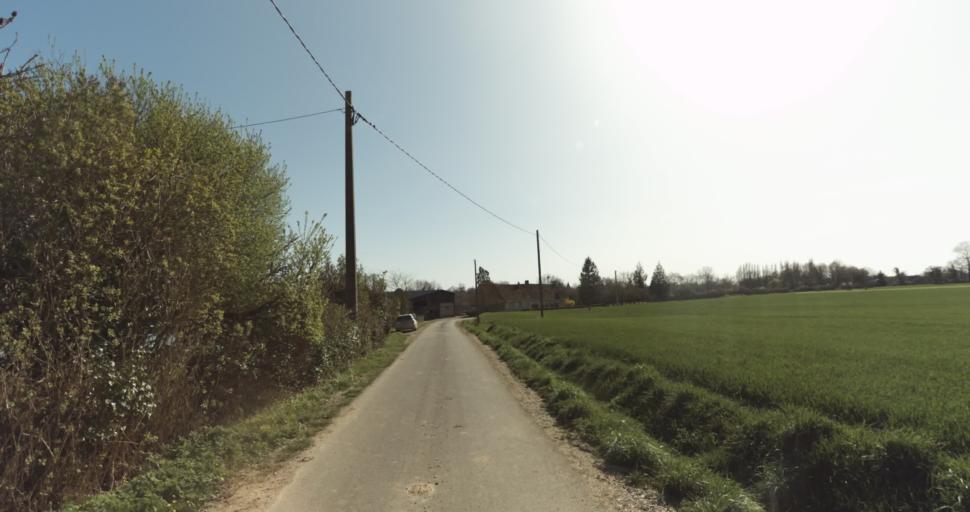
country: FR
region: Lower Normandy
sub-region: Departement du Calvados
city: Saint-Pierre-sur-Dives
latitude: 48.9382
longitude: 0.0083
